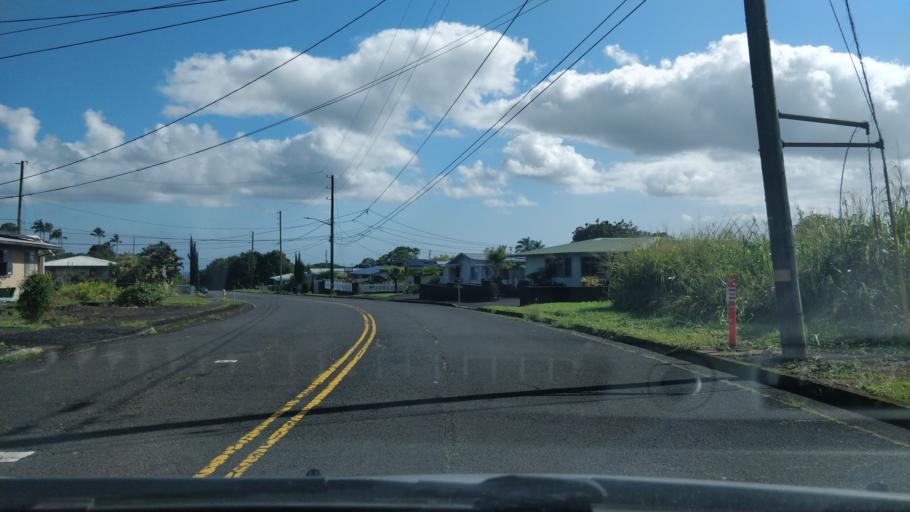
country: US
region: Hawaii
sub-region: Hawaii County
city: Hilo
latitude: 19.6787
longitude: -155.0887
